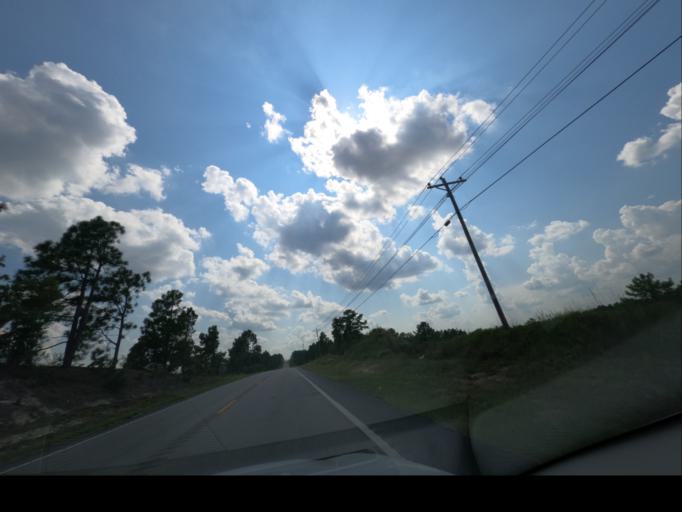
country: US
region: South Carolina
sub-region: Lexington County
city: South Congaree
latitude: 33.8797
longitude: -81.1760
